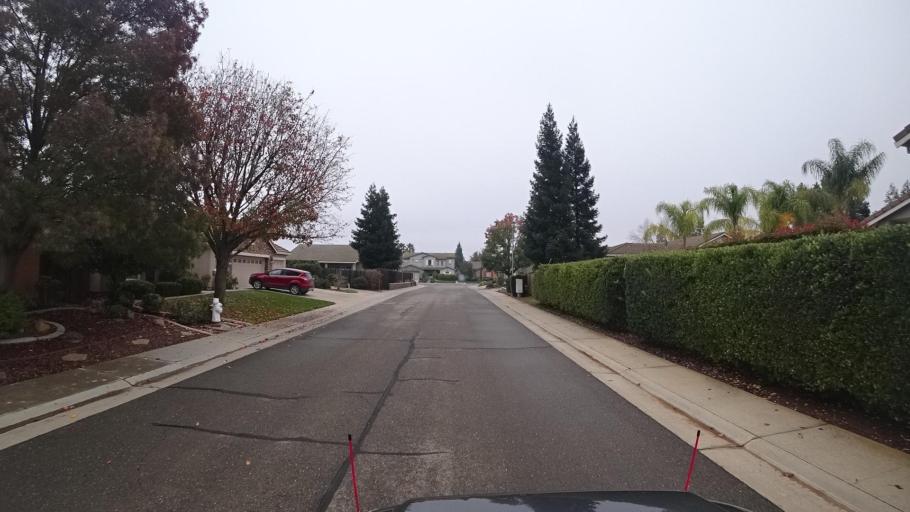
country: US
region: California
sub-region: Sacramento County
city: Elk Grove
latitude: 38.4069
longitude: -121.3371
